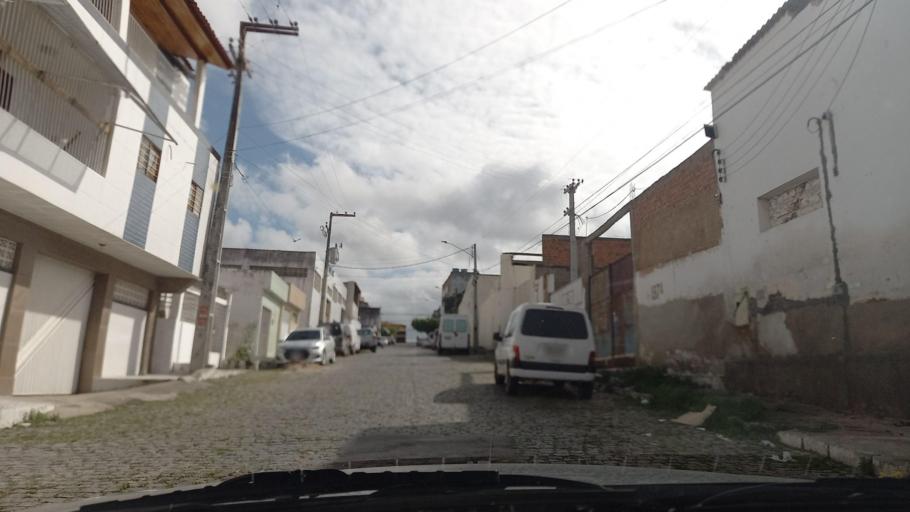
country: BR
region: Pernambuco
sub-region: Caruaru
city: Caruaru
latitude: -8.2871
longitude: -35.9821
